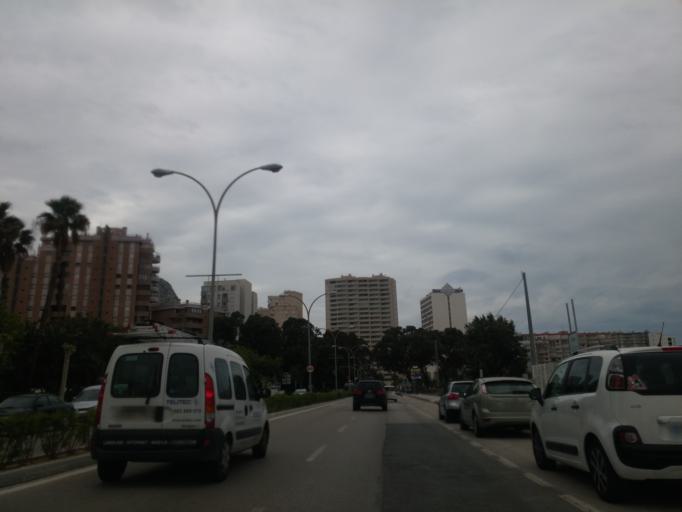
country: ES
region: Valencia
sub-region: Provincia de Alicante
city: Calp
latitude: 38.6457
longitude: 0.0712
